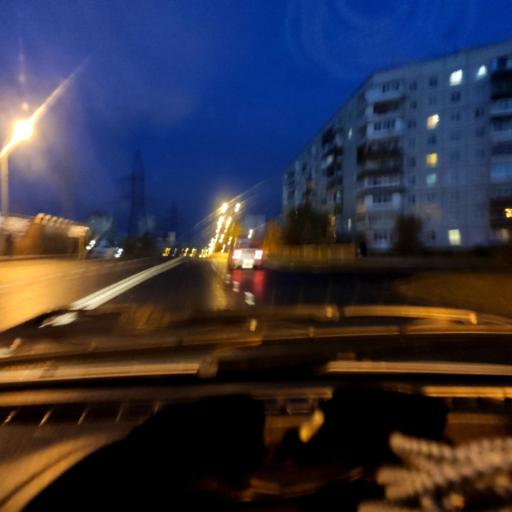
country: RU
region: Samara
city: Zhigulevsk
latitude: 53.4716
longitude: 49.5311
